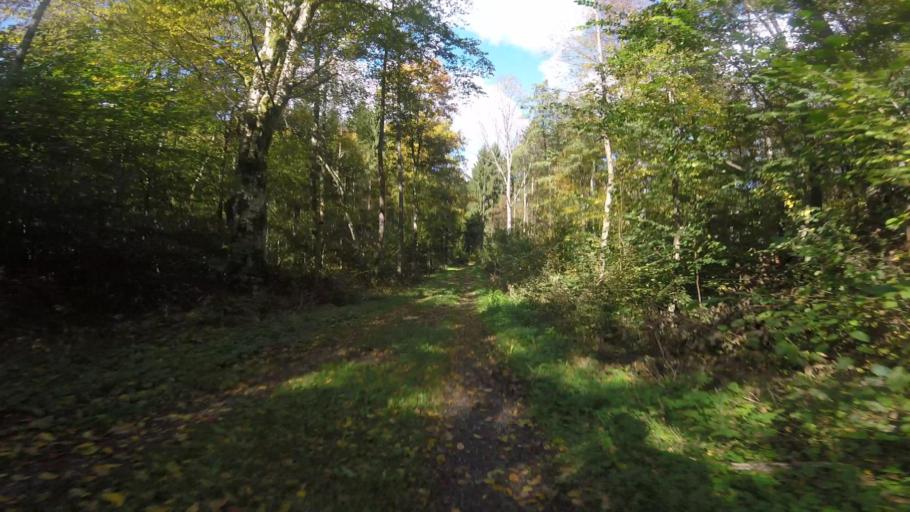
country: DE
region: Baden-Wuerttemberg
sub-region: Regierungsbezirk Stuttgart
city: Aspach
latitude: 48.9832
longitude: 9.3896
